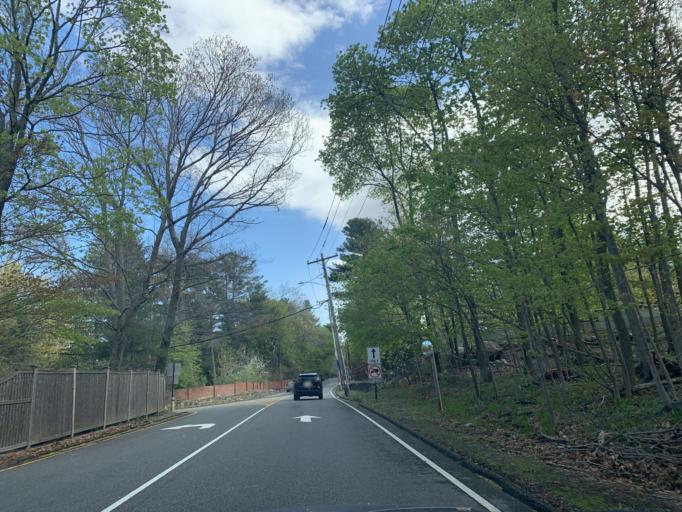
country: US
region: Massachusetts
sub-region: Norfolk County
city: Dedham
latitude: 42.2221
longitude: -71.1179
